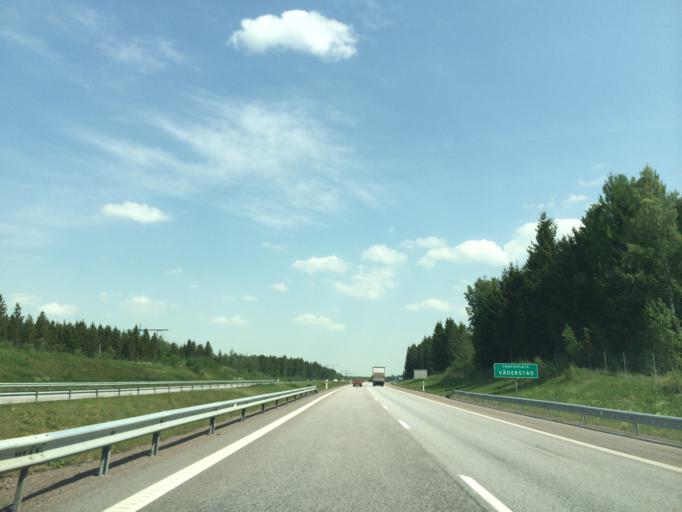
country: SE
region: OEstergoetland
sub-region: Vadstena Kommun
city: Herrestad
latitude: 58.2922
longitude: 14.9015
